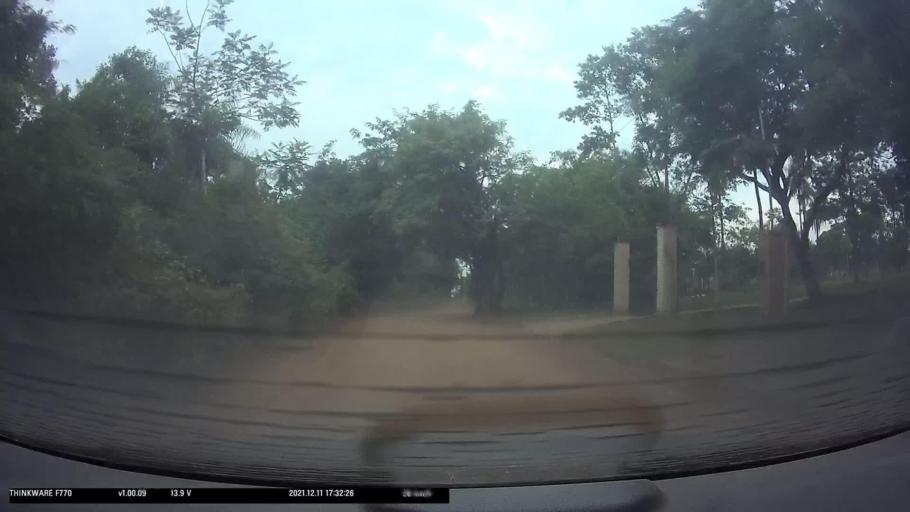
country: PY
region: Cordillera
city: Altos
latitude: -25.3028
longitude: -57.2431
